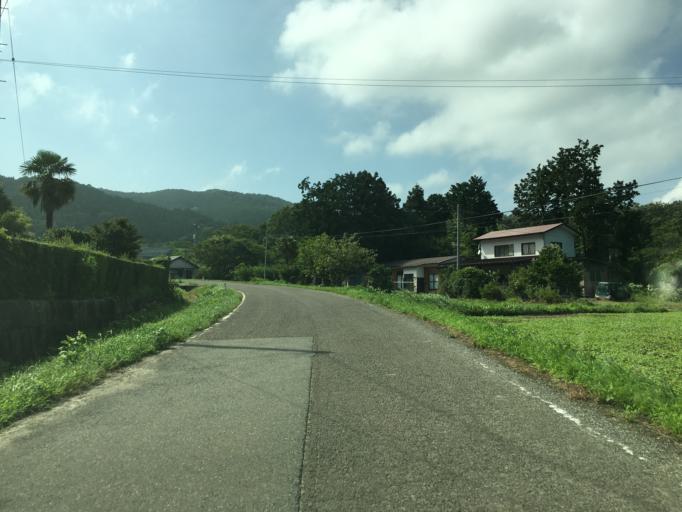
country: JP
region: Miyagi
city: Marumori
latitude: 37.8913
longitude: 140.8777
